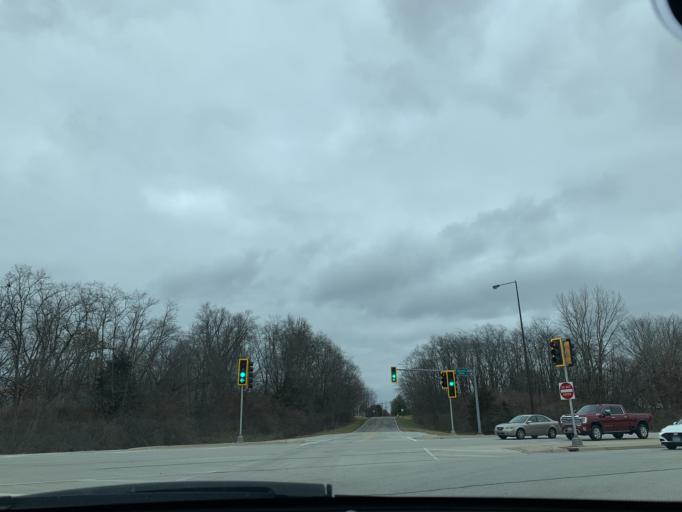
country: US
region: Illinois
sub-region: Sangamon County
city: Leland Grove
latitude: 39.8251
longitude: -89.6873
